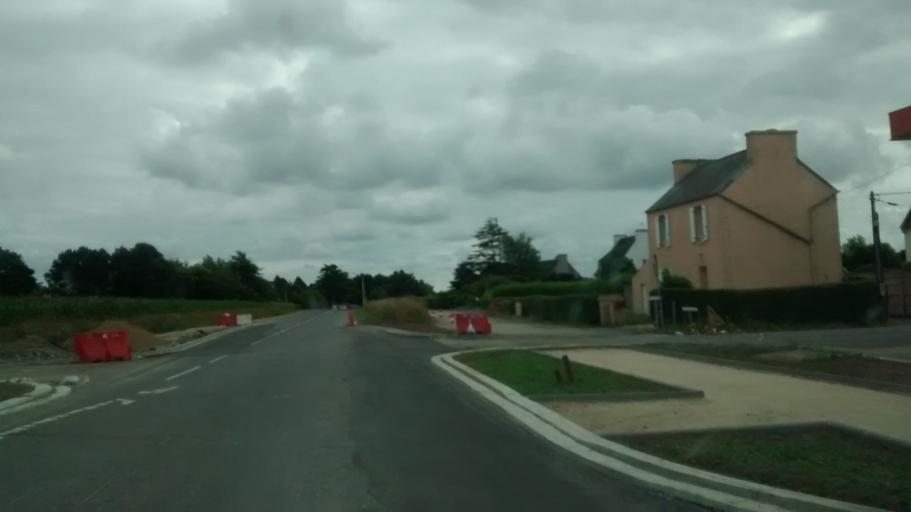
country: FR
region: Brittany
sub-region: Departement du Finistere
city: Le Folgoet
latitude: 48.5578
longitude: -4.3407
